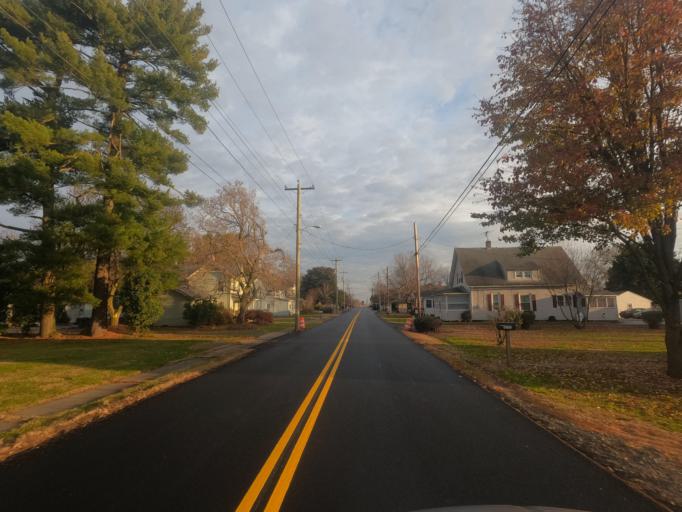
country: US
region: Delaware
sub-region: New Castle County
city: Townsend
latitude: 39.3080
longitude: -75.8263
